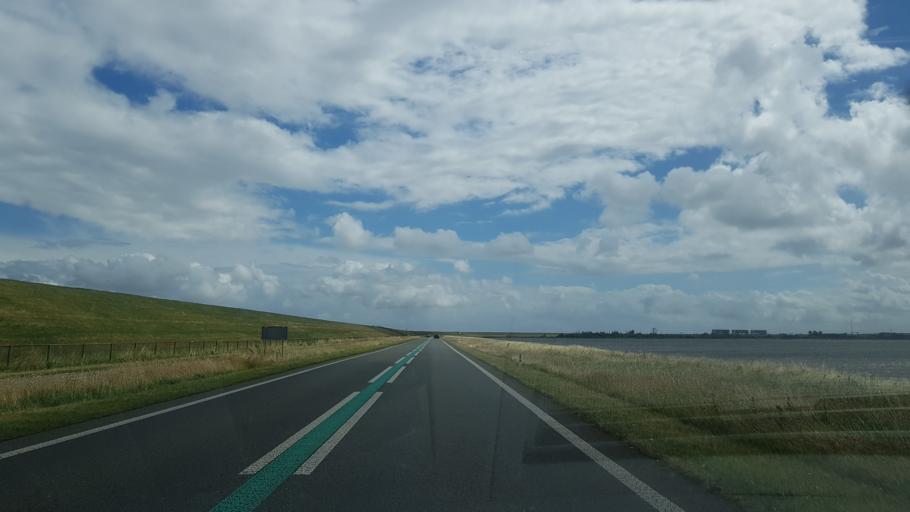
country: NL
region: Friesland
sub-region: Gemeente Dongeradeel
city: Anjum
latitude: 53.4098
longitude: 6.1627
